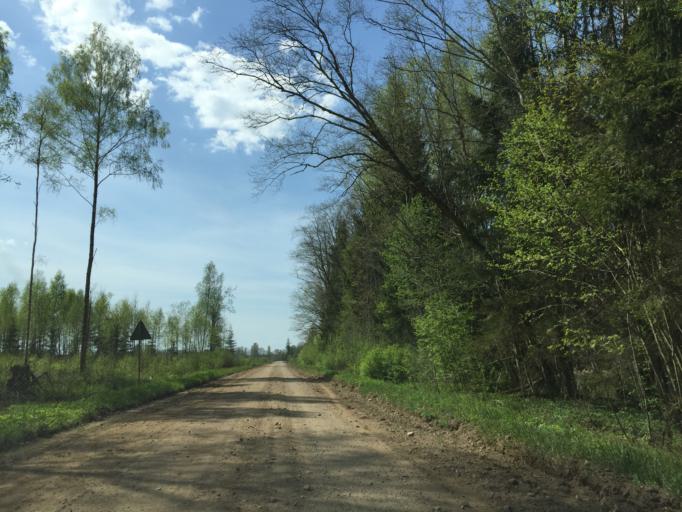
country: LV
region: Limbazu Rajons
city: Limbazi
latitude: 57.3876
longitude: 24.5937
